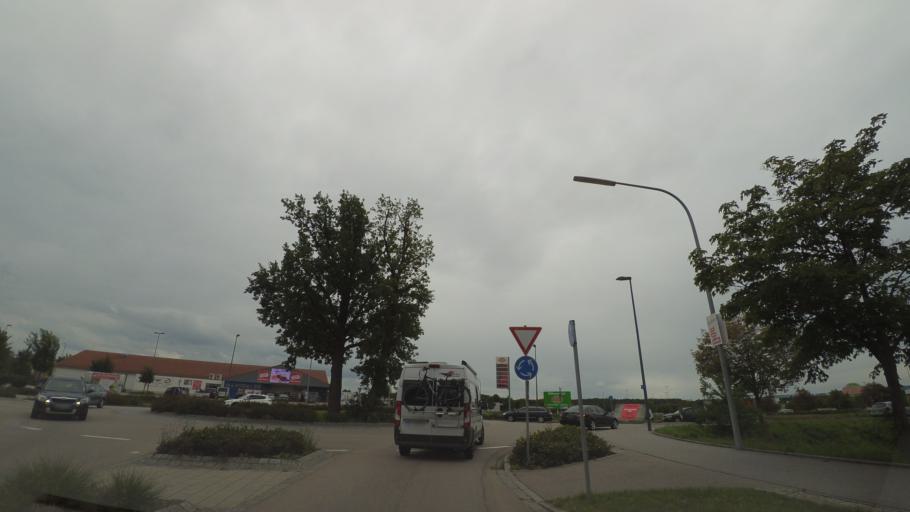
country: DE
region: Bavaria
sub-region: Upper Palatinate
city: Wackersdorf
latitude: 49.3147
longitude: 12.1483
